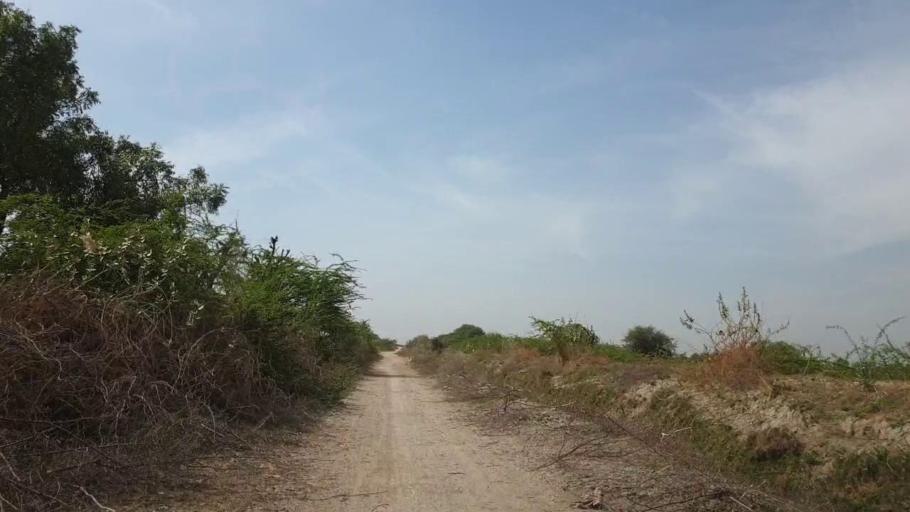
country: PK
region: Sindh
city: Kunri
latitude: 25.1946
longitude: 69.5687
